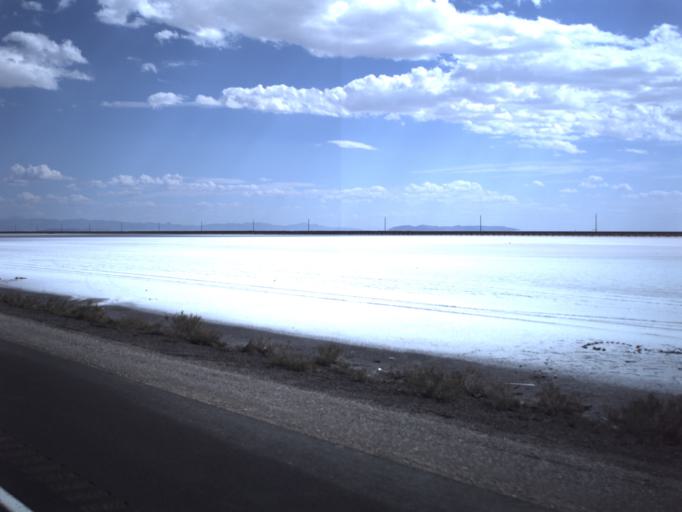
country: US
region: Utah
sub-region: Tooele County
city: Wendover
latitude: 40.7341
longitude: -113.6415
